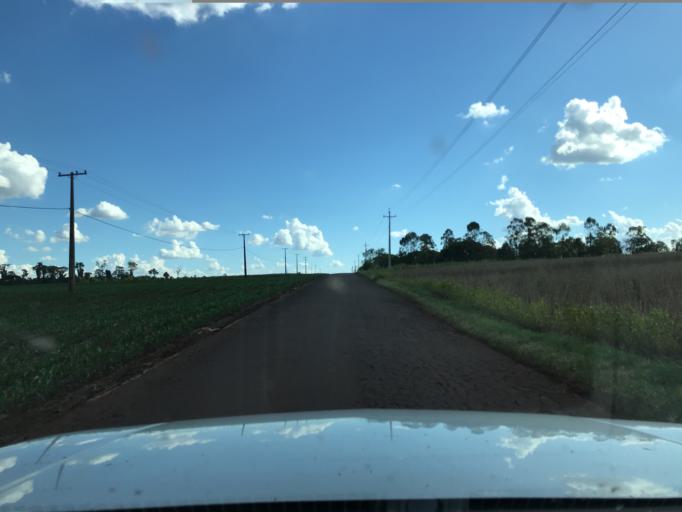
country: BR
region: Parana
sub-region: Palotina
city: Palotina
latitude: -24.2683
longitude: -53.8050
